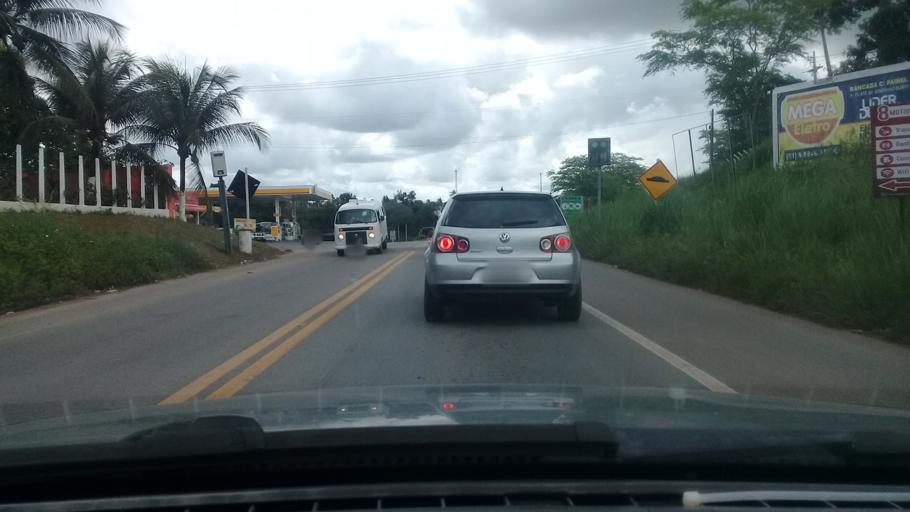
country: BR
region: Pernambuco
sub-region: Nazare Da Mata
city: Nazare da Mata
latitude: -7.7553
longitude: -35.2330
